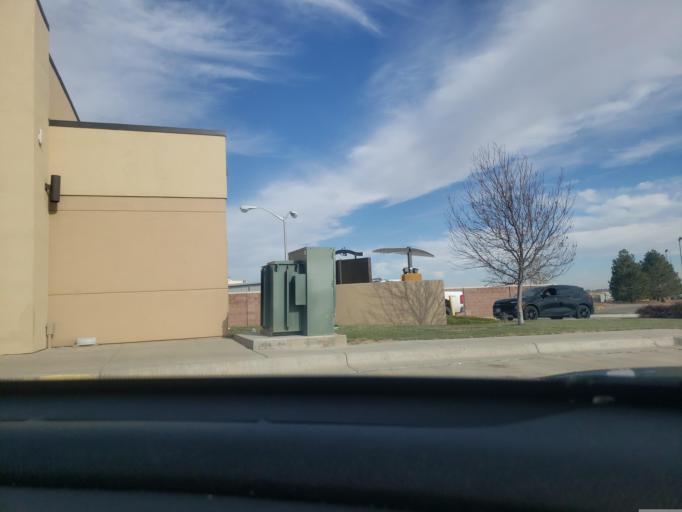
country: US
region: Kansas
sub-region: Finney County
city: Garden City
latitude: 37.9790
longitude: -100.8415
